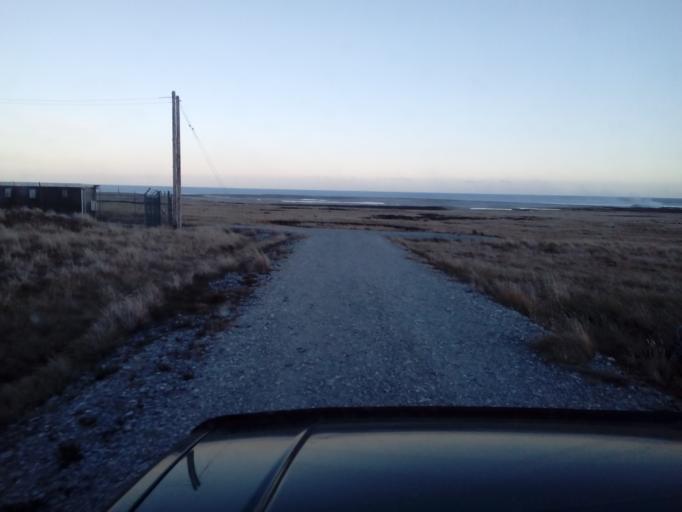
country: FK
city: Stanley
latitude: -51.7051
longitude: -57.8433
